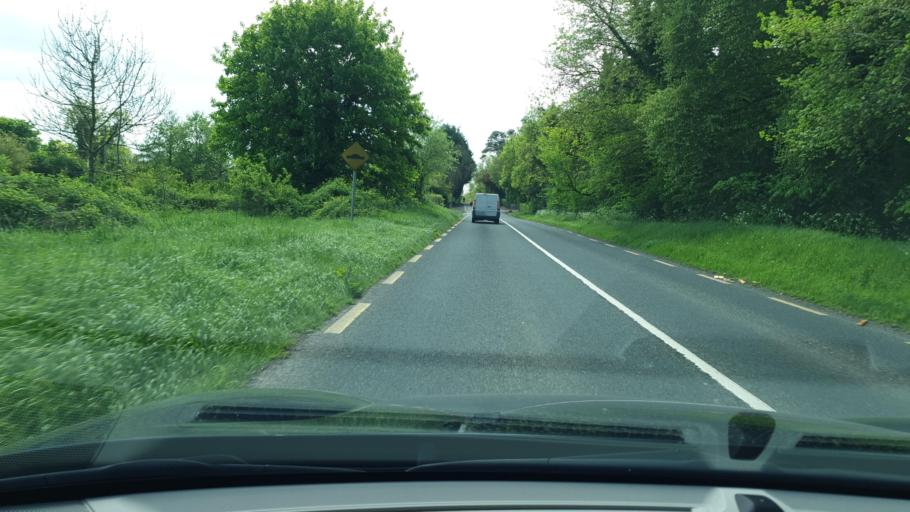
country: IE
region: Leinster
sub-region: An Mhi
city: Navan
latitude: 53.7496
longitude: -6.7192
